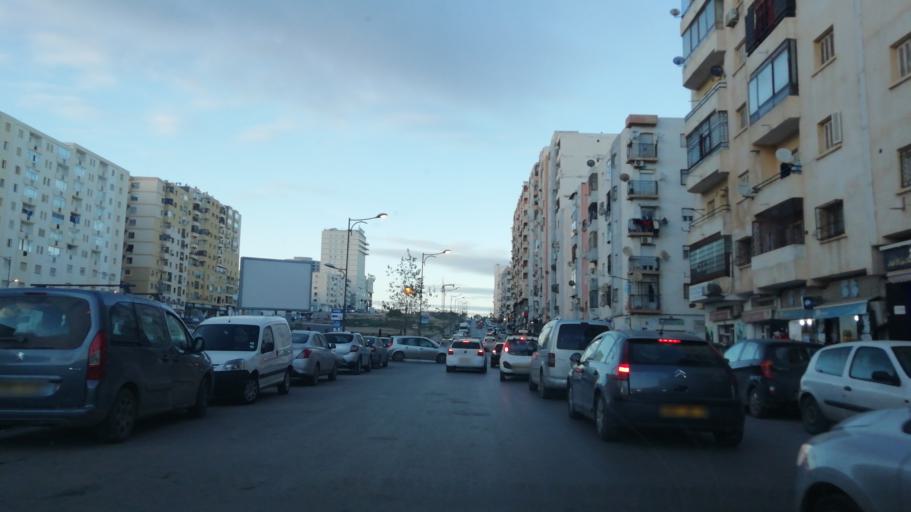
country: DZ
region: Oran
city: Bir el Djir
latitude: 35.7028
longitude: -0.5607
